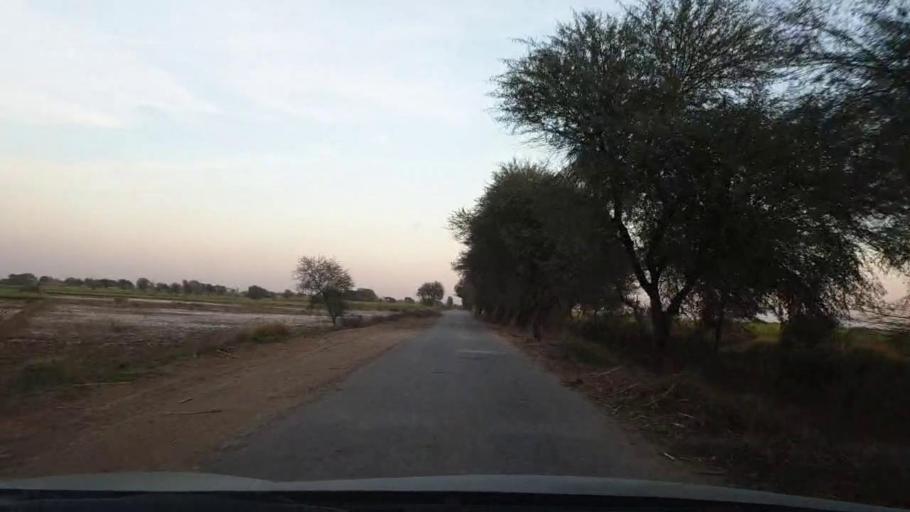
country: PK
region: Sindh
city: Tando Allahyar
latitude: 25.5980
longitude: 68.6997
